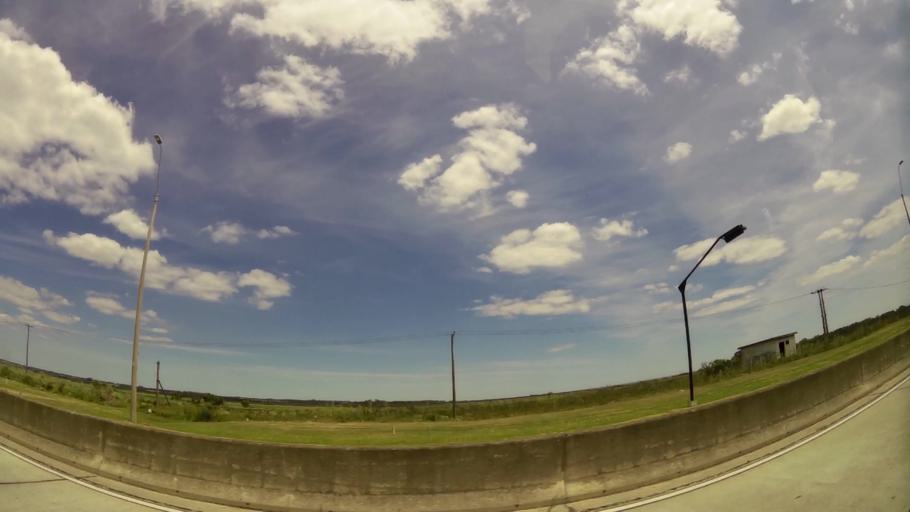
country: UY
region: San Jose
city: Delta del Tigre
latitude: -34.7728
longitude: -56.3823
